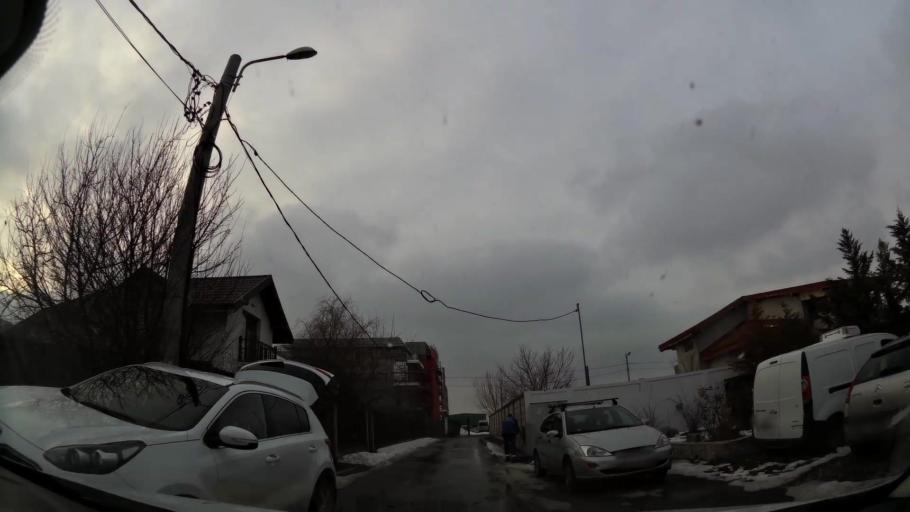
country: RO
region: Ilfov
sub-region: Voluntari City
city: Voluntari
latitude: 44.4980
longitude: 26.1629
